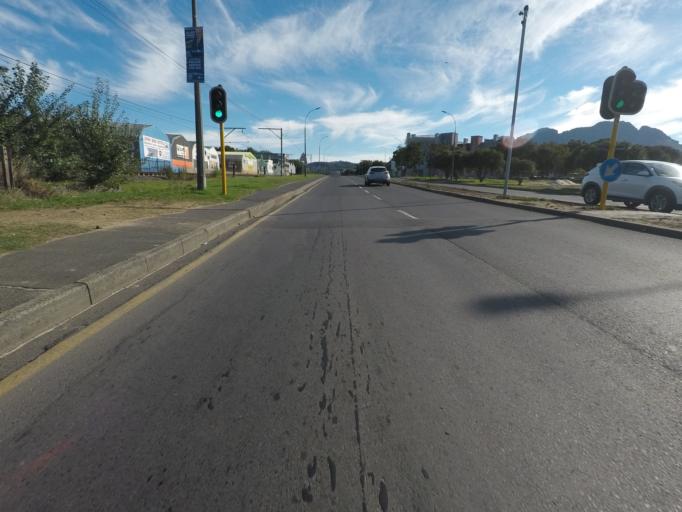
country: ZA
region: Western Cape
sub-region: Cape Winelands District Municipality
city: Stellenbosch
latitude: -33.9327
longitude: 18.8527
